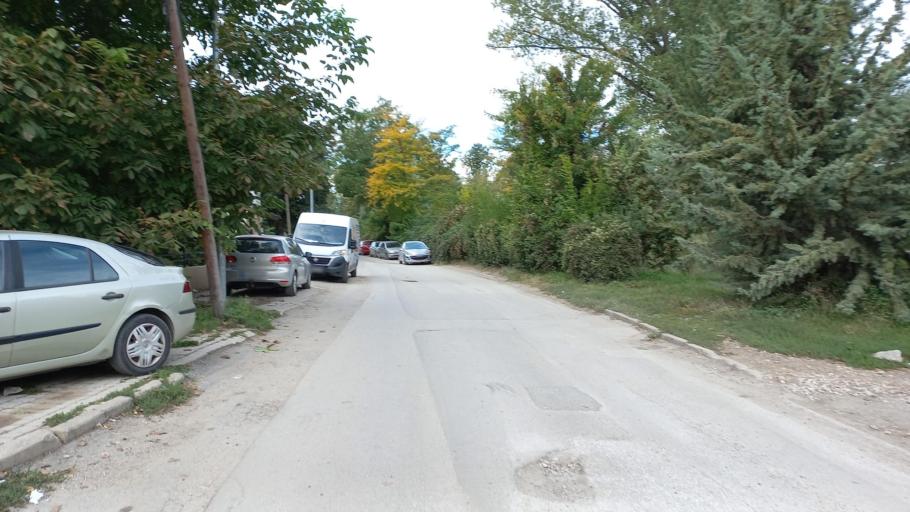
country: MK
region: Kumanovo
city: Kumanovo
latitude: 42.1410
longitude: 21.7175
